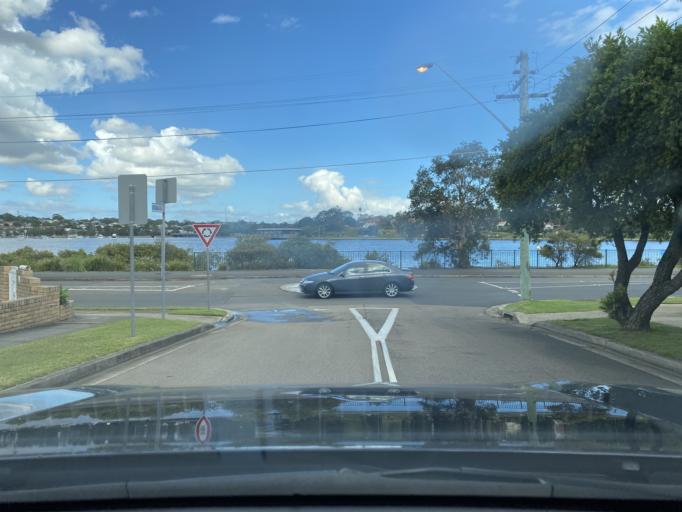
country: AU
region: New South Wales
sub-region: Leichhardt
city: Leichhardt
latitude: -33.8664
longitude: 151.1460
